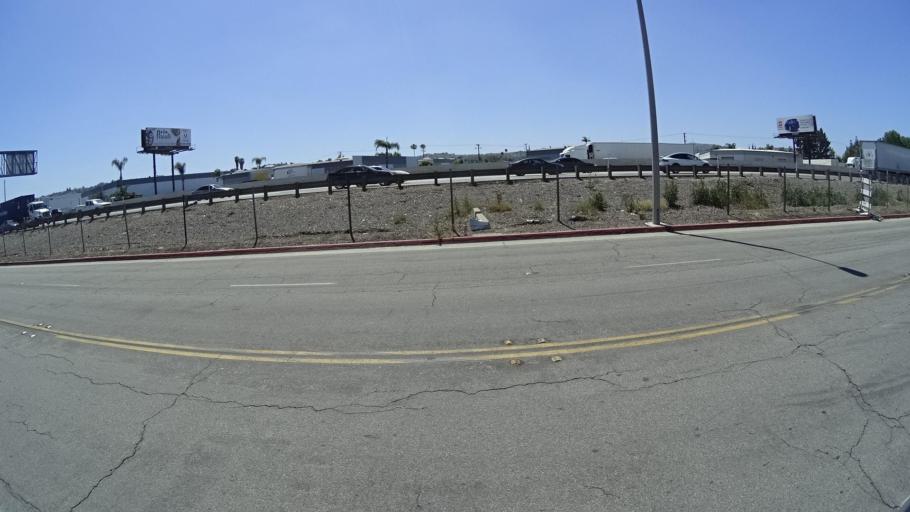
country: US
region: California
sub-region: Los Angeles County
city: Walnut
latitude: 33.9958
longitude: -117.8767
